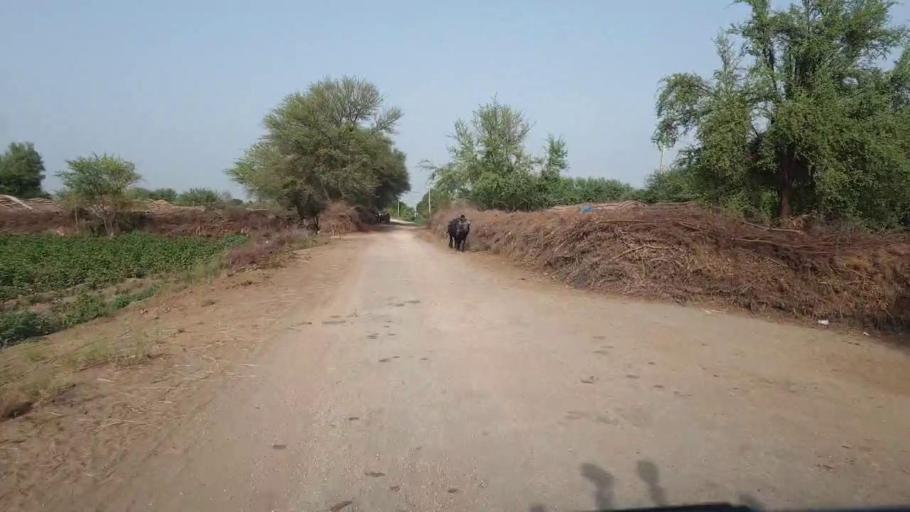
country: PK
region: Sindh
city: Daur
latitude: 26.3399
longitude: 68.2517
